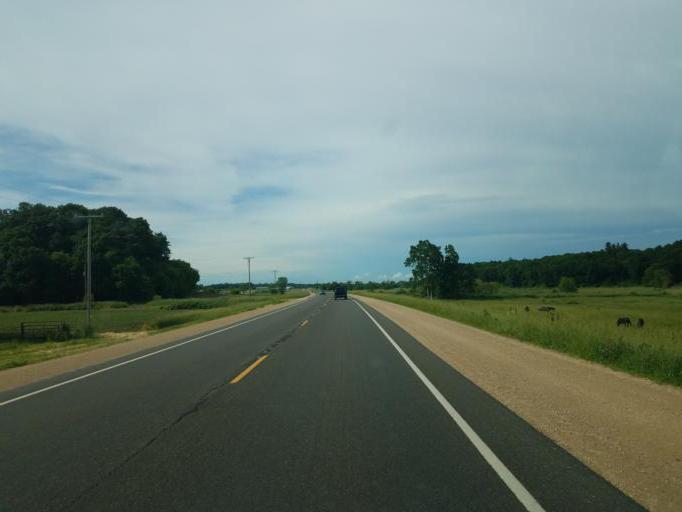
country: US
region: Wisconsin
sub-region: Monroe County
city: Tomah
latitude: 43.9382
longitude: -90.5028
